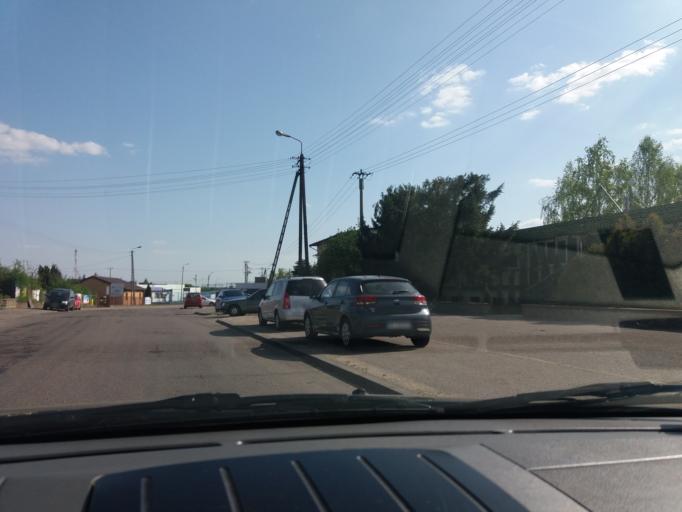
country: PL
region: Masovian Voivodeship
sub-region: Powiat mlawski
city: Mlawa
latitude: 53.1185
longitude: 20.3586
